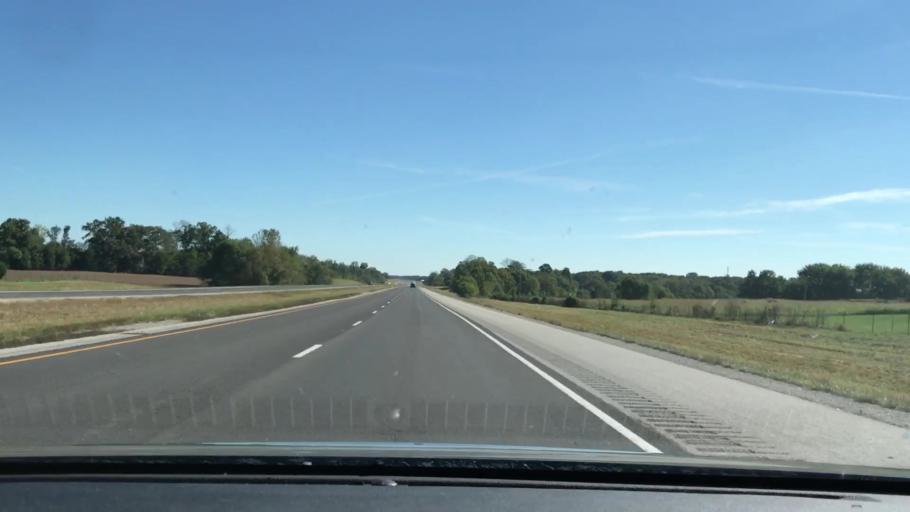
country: US
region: Kentucky
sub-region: Todd County
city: Elkton
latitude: 36.8028
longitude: -87.0877
